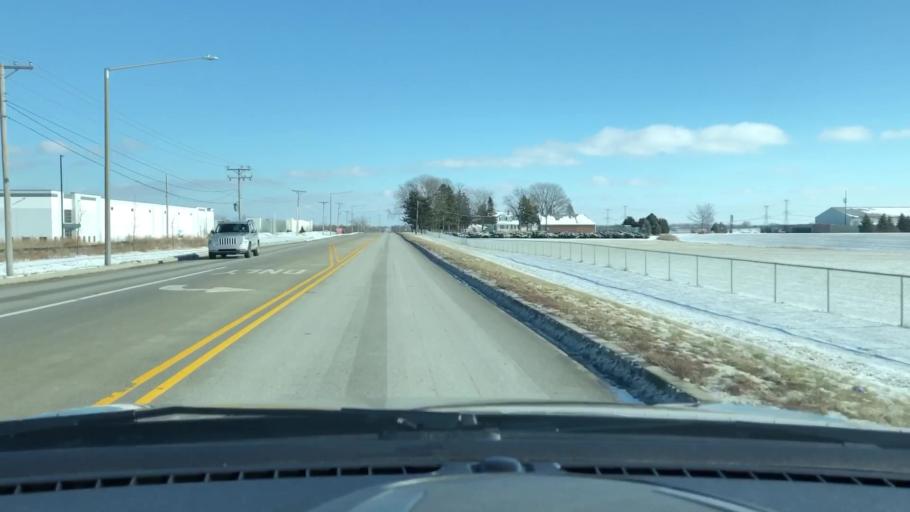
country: US
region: Illinois
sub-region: Will County
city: Preston Heights
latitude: 41.4812
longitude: -88.0597
